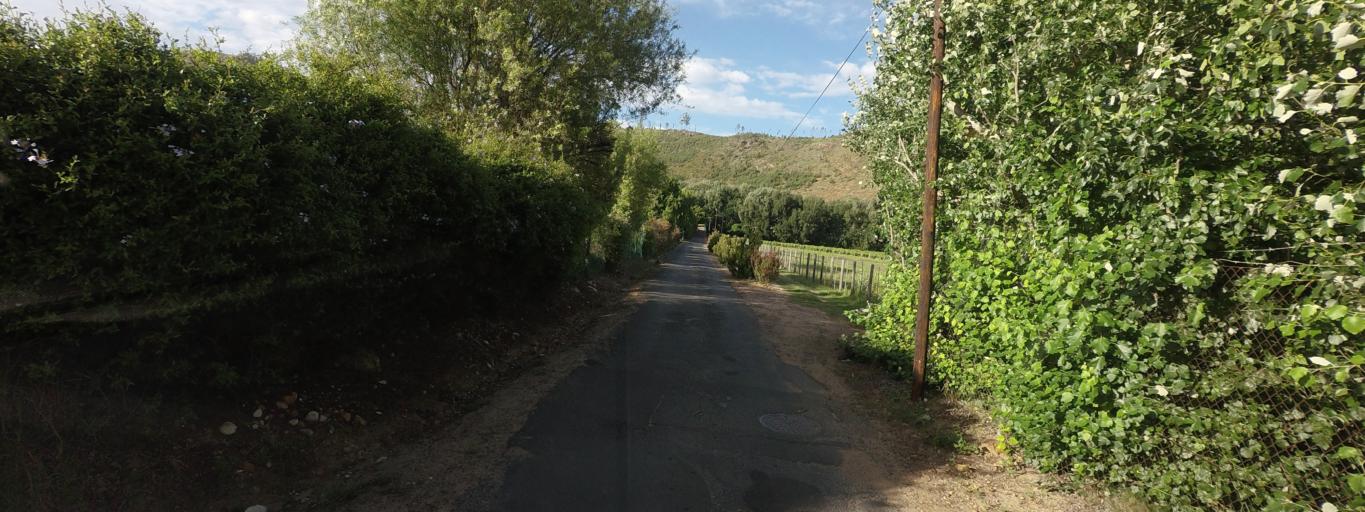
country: ZA
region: Western Cape
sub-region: Cape Winelands District Municipality
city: Paarl
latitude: -33.8973
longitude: 19.0946
